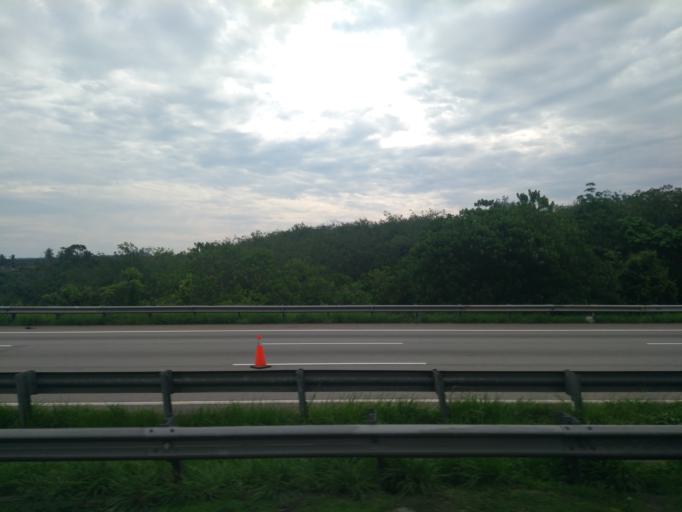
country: MY
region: Melaka
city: Alor Gajah
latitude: 2.4152
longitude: 102.2170
